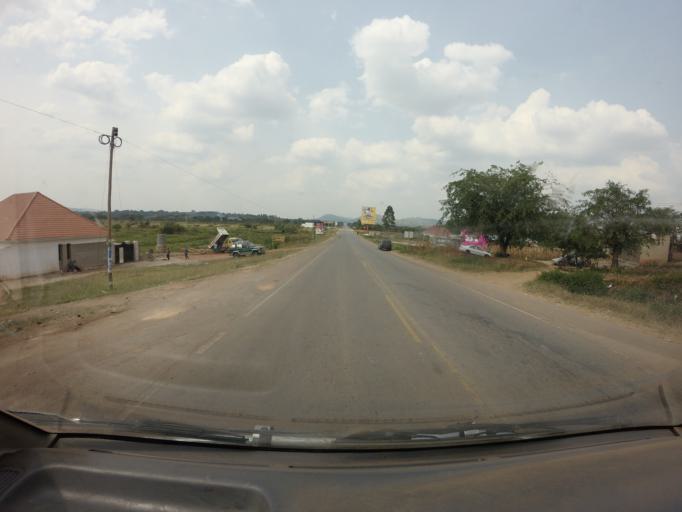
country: UG
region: Central Region
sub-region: Lyantonde District
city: Lyantonde
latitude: -0.4032
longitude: 31.1605
